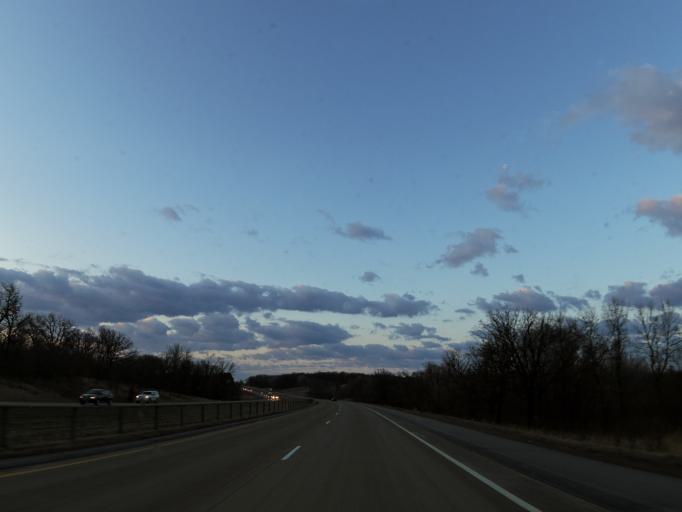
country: US
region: Minnesota
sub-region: Scott County
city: Elko New Market
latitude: 44.5360
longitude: -93.3014
